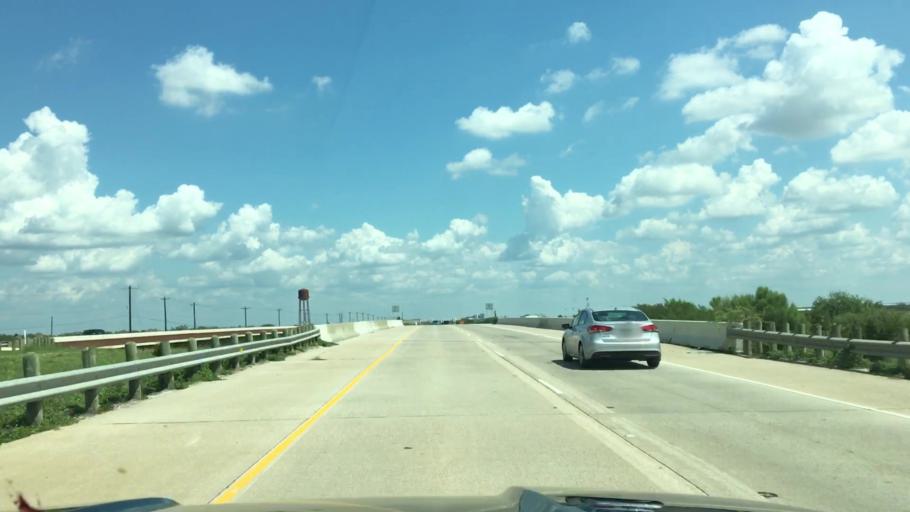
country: US
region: Texas
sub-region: Tarrant County
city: Haslet
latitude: 33.0352
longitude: -97.3422
